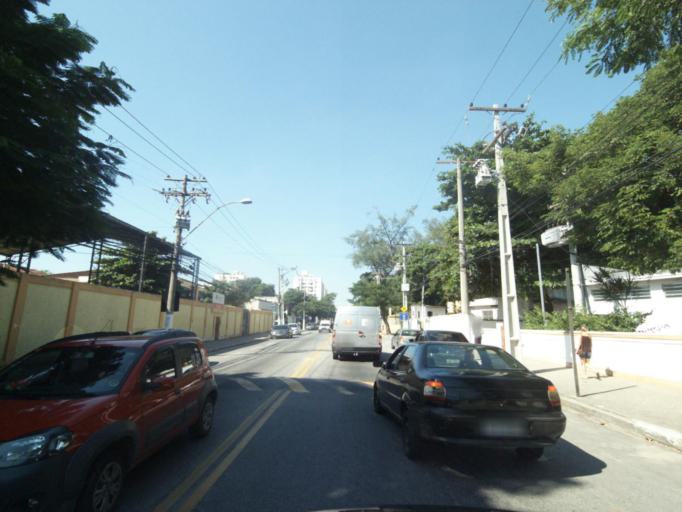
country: BR
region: Rio de Janeiro
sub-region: Niteroi
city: Niteroi
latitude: -22.8648
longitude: -43.0998
